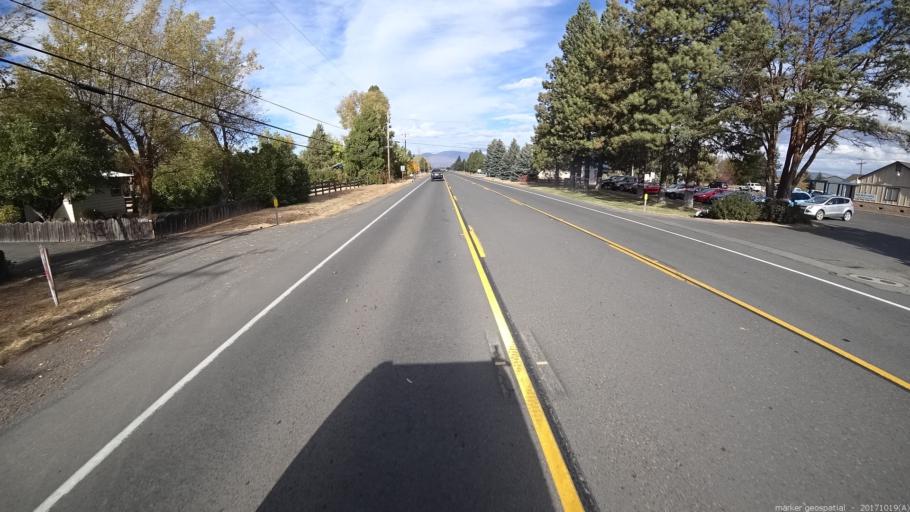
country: US
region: California
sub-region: Shasta County
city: Burney
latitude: 41.0243
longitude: -121.4244
